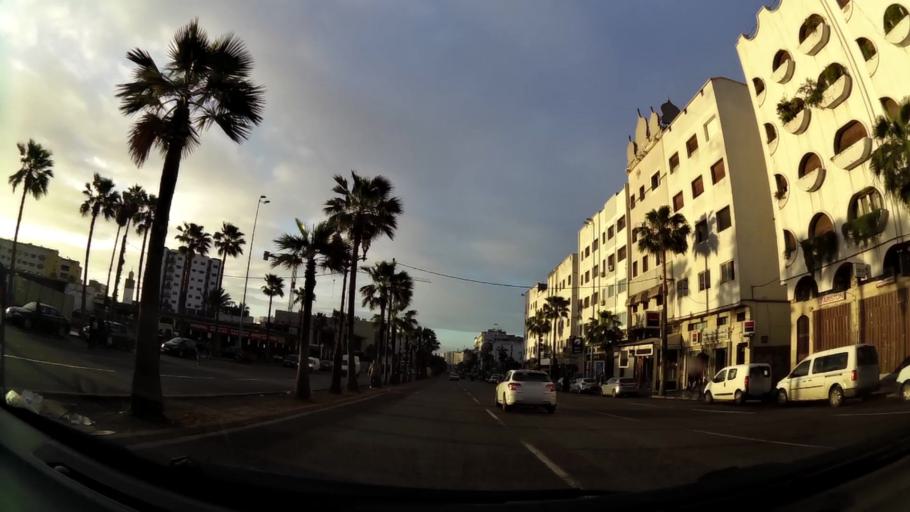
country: MA
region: Grand Casablanca
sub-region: Casablanca
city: Casablanca
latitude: 33.5636
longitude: -7.5951
